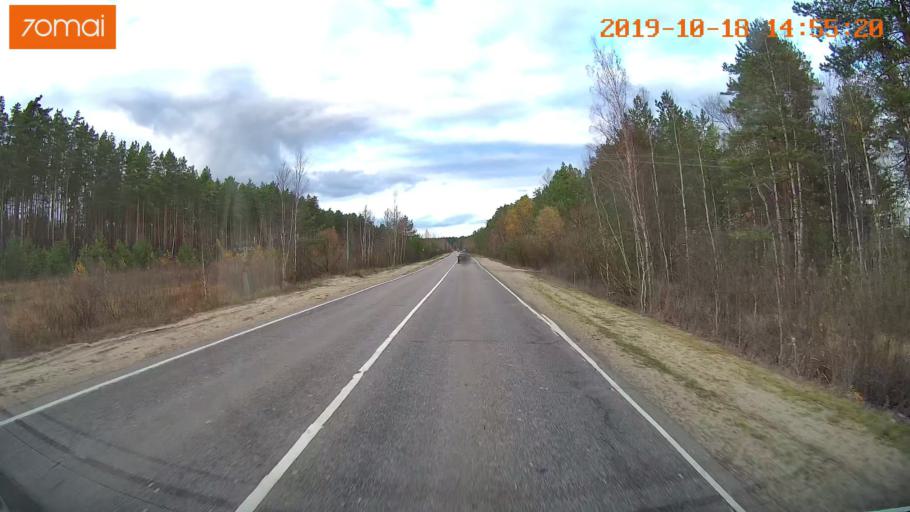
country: RU
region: Vladimir
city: Kurlovo
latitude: 55.4507
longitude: 40.5887
